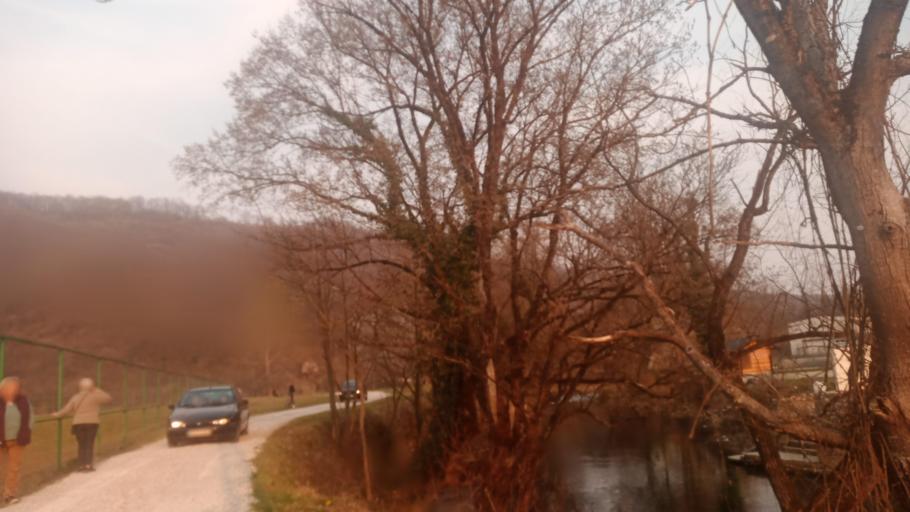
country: BA
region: Federation of Bosnia and Herzegovina
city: Bosanska Krupa
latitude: 44.8869
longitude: 16.1593
